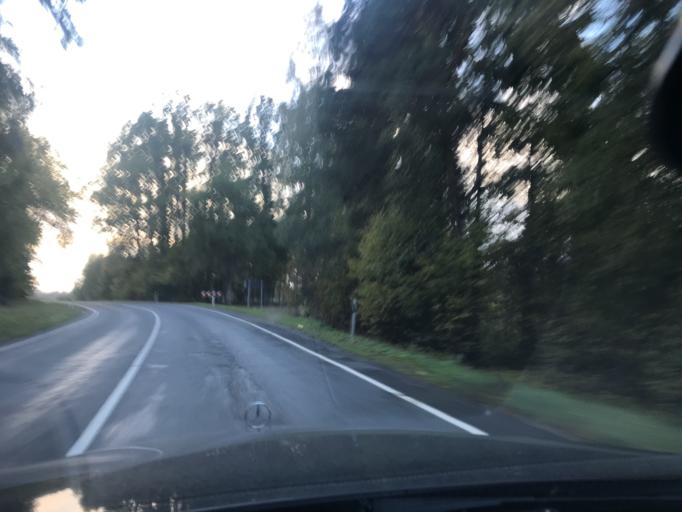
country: EE
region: Vorumaa
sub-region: Antsla vald
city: Vana-Antsla
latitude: 57.8835
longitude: 26.5631
